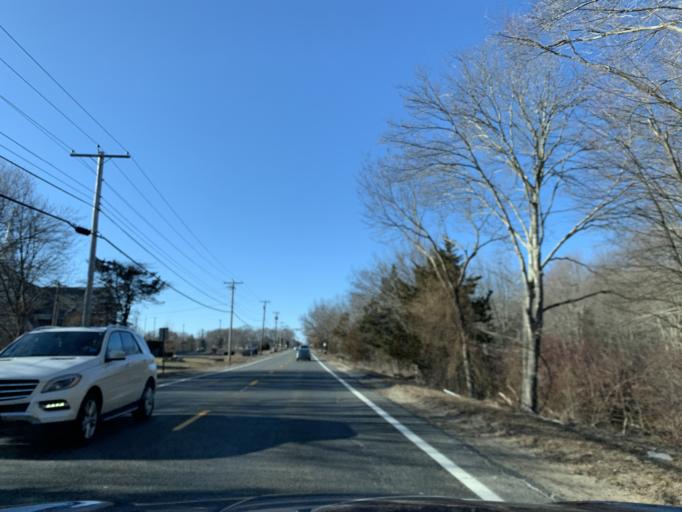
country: US
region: Rhode Island
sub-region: Providence County
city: Smithfield
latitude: 41.8998
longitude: -71.5020
